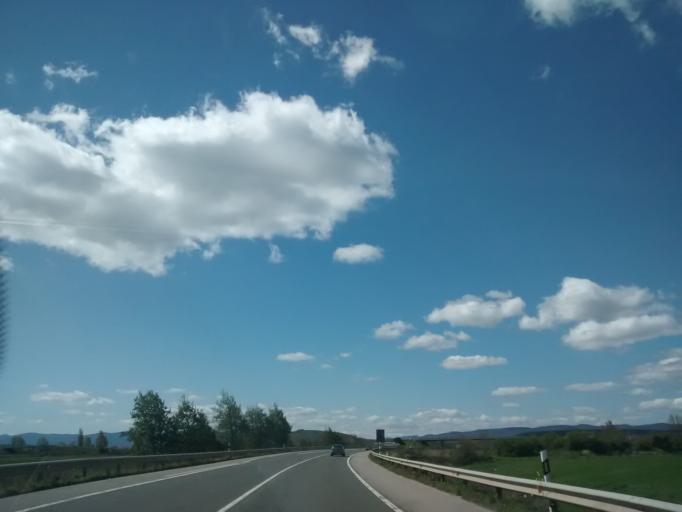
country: ES
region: Basque Country
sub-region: Provincia de Alava
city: Zambrana
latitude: 42.6562
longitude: -2.8809
